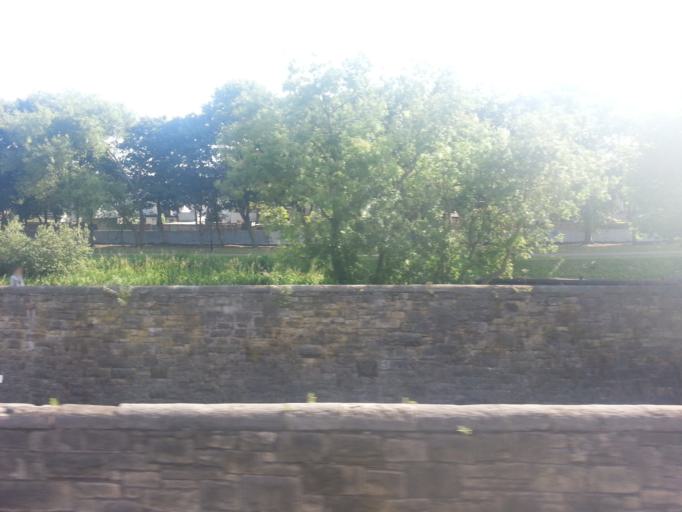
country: IE
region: Leinster
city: Drumcondra
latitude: 53.3626
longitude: -6.2631
